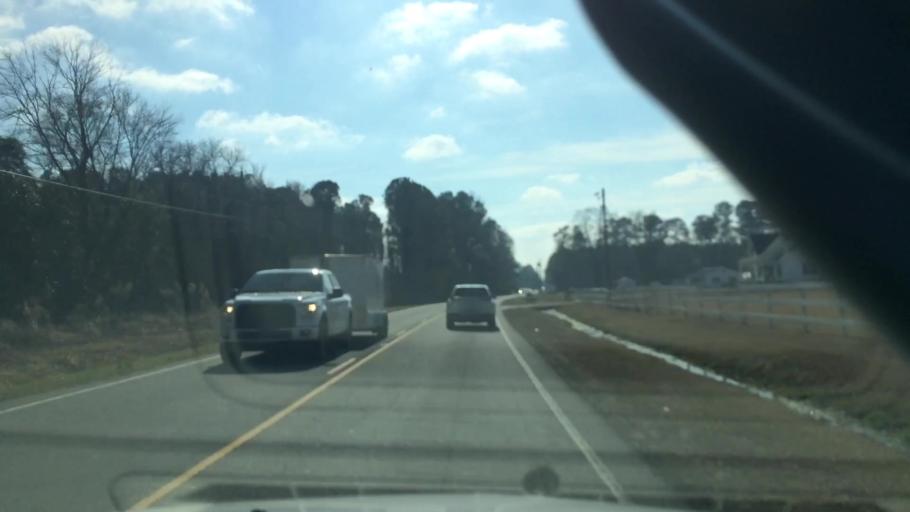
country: US
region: North Carolina
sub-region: Duplin County
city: Beulaville
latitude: 34.8698
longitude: -77.7920
